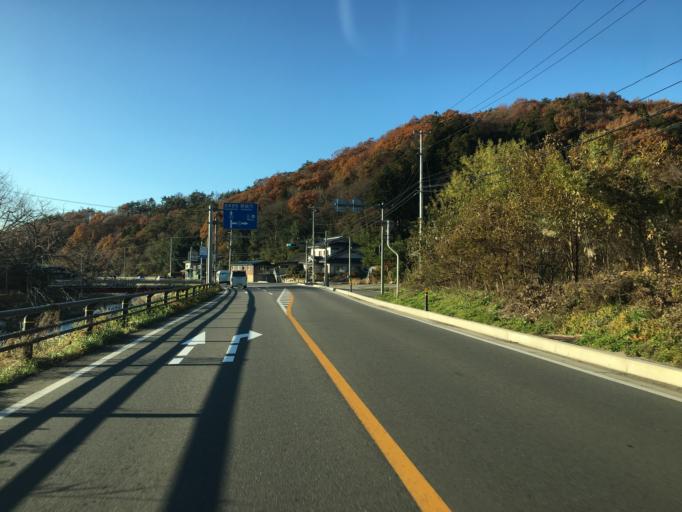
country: JP
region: Fukushima
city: Sukagawa
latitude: 37.3104
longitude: 140.4846
